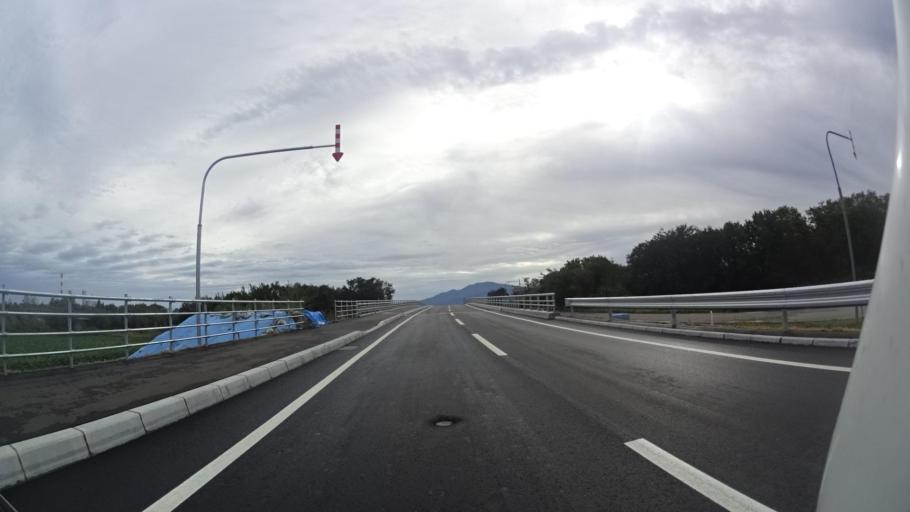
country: JP
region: Hokkaido
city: Abashiri
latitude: 43.8702
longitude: 144.6477
